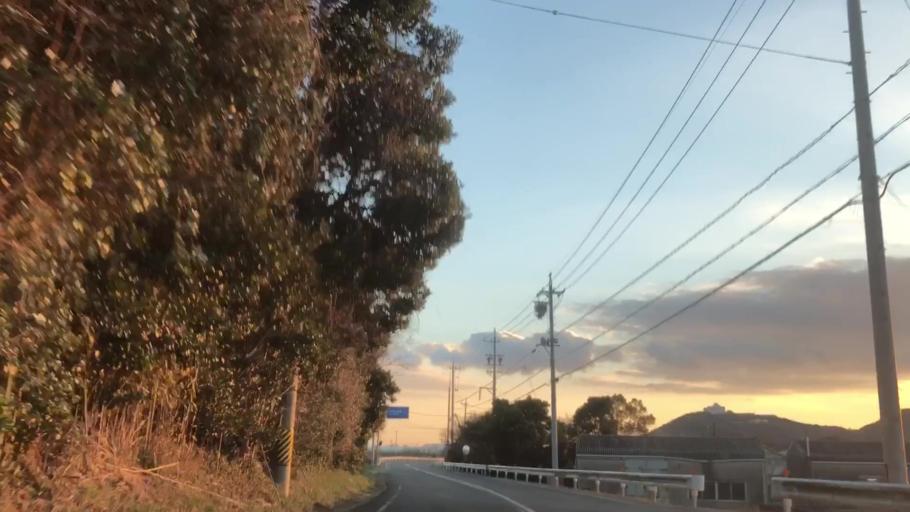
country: JP
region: Aichi
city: Toyohama
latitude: 34.5961
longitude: 137.0485
